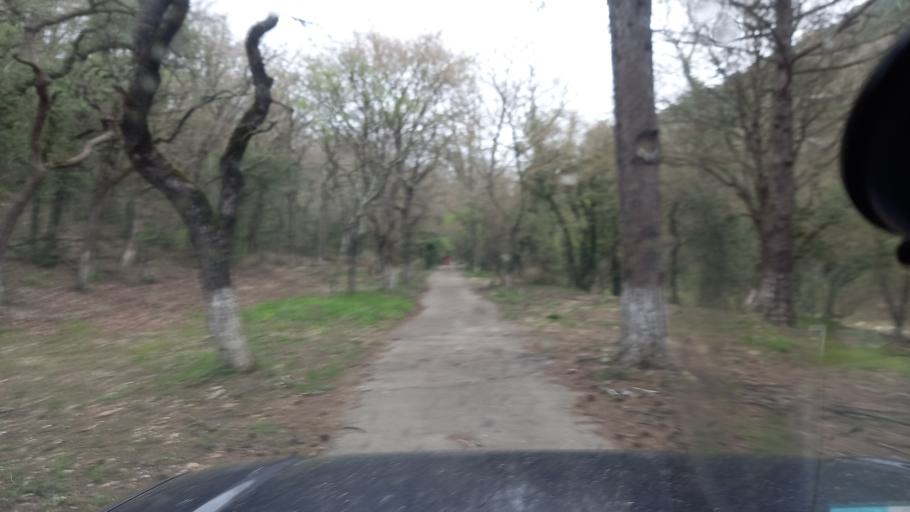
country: RU
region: Krasnodarskiy
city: Arkhipo-Osipovka
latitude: 44.3705
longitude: 38.4499
